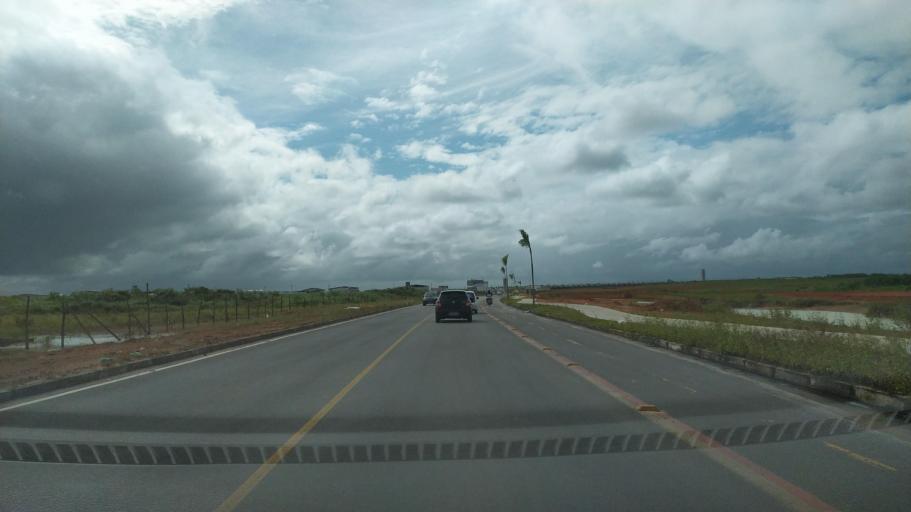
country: BR
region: Alagoas
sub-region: Satuba
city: Satuba
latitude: -9.5389
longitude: -35.7657
